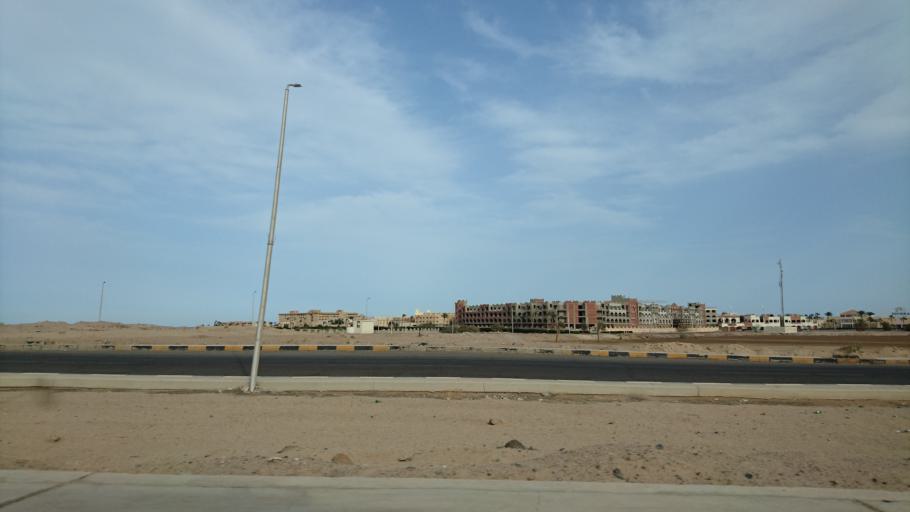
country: EG
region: Red Sea
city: Bur Safajah
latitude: 26.8018
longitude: 33.9369
